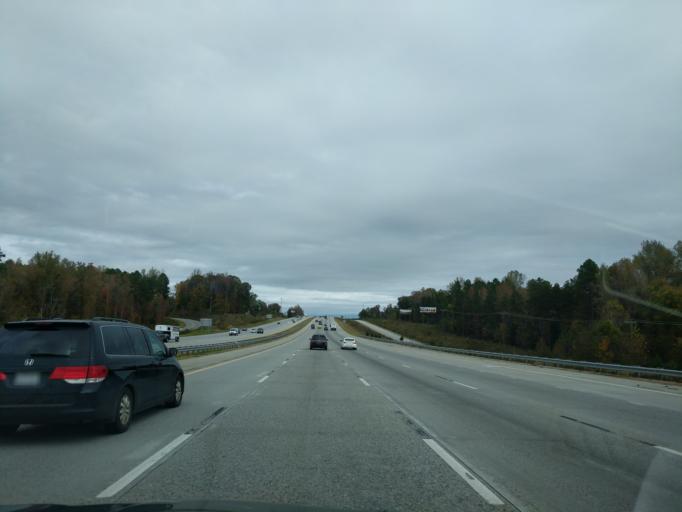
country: US
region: North Carolina
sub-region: Rowan County
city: Spencer
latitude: 35.7009
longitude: -80.3991
